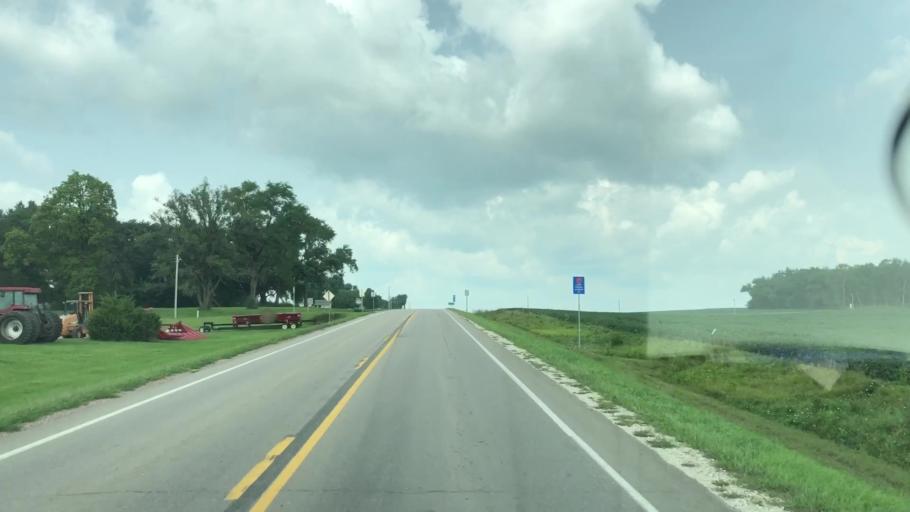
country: US
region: Iowa
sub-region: Plymouth County
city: Kingsley
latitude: 42.5872
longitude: -95.9575
